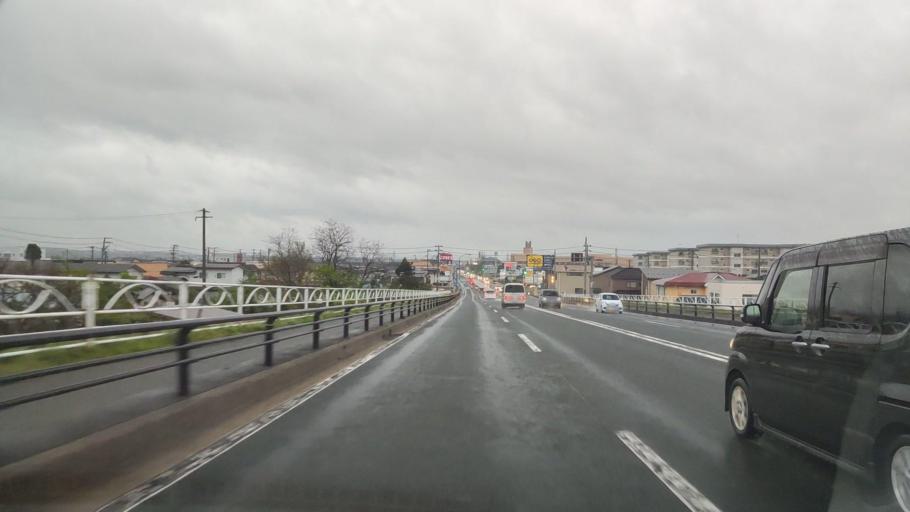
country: JP
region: Akita
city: Akita
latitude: 39.6965
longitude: 140.1190
